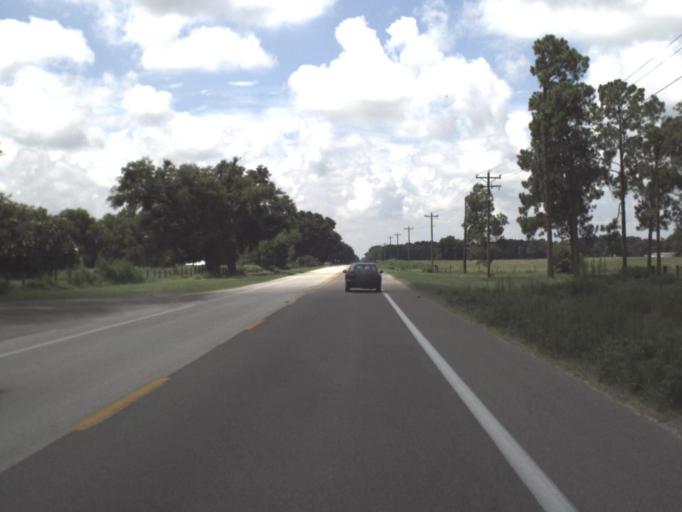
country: US
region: Florida
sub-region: Gilchrist County
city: Trenton
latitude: 29.7280
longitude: -82.8578
